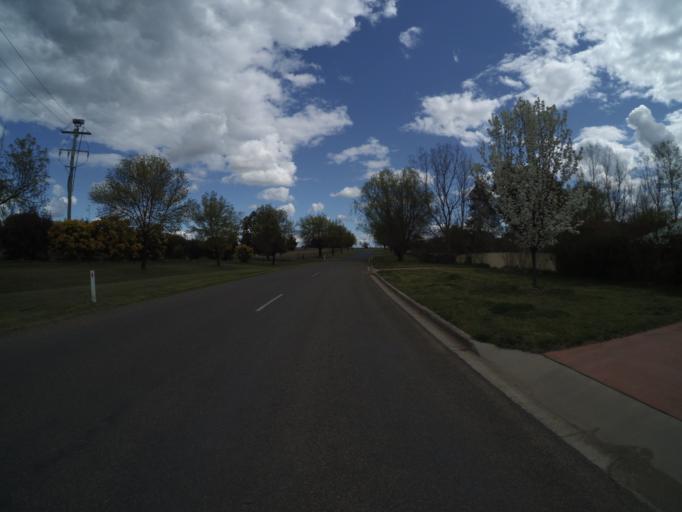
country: AU
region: New South Wales
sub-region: Yass Valley
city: Yass
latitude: -34.8581
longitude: 148.9183
